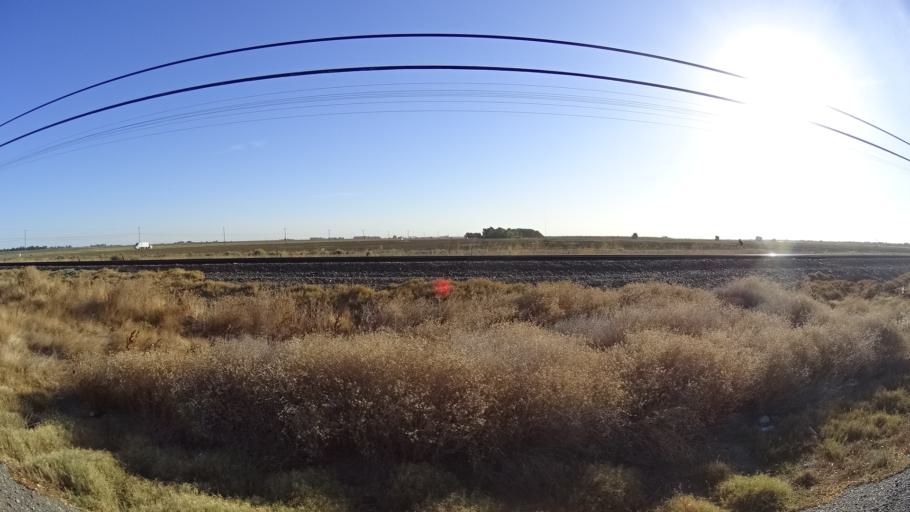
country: US
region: California
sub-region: Yolo County
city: Davis
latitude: 38.5884
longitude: -121.7519
